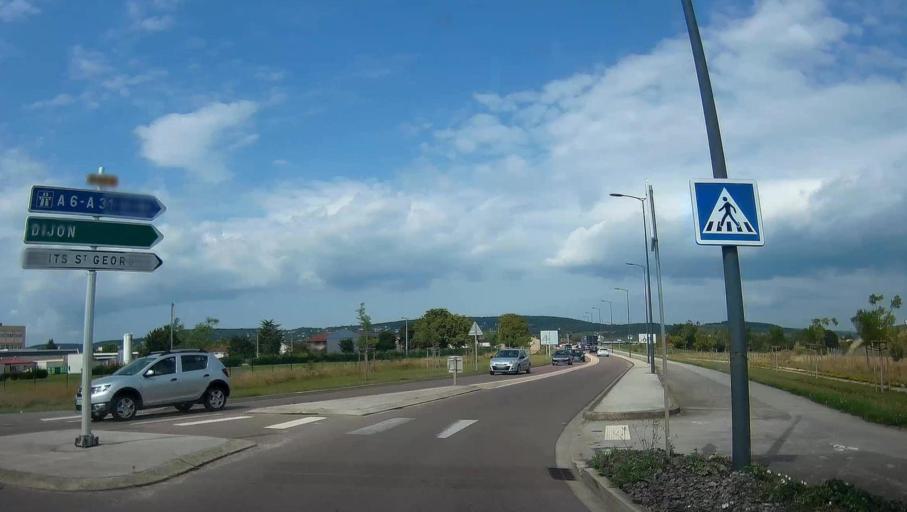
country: FR
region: Bourgogne
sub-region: Departement de la Cote-d'Or
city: Beaune
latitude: 47.0383
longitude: 4.8512
